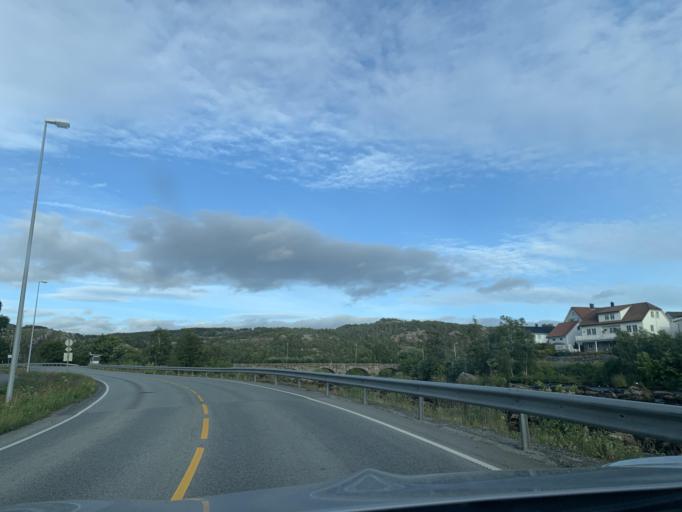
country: NO
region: Rogaland
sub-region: Eigersund
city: Egersund
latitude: 58.4605
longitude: 6.0127
